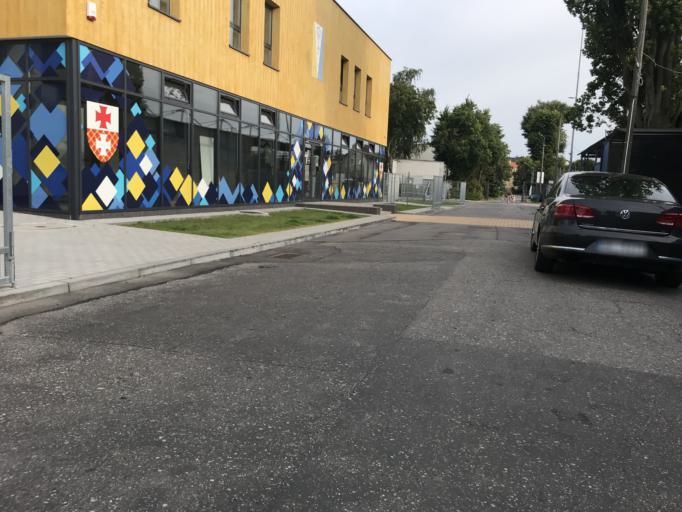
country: PL
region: Warmian-Masurian Voivodeship
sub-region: Powiat elblaski
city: Elblag
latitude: 54.1661
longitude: 19.4221
